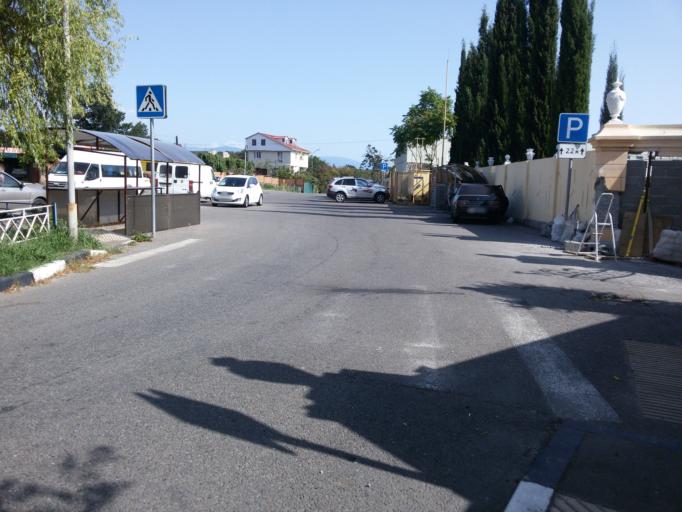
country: RU
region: Krasnodarskiy
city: Adler
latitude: 43.4187
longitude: 39.9383
